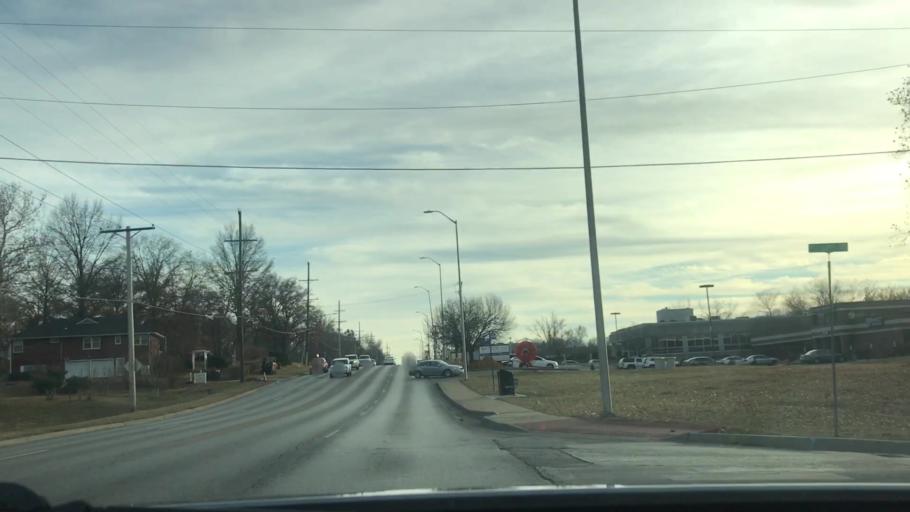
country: US
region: Missouri
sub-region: Clay County
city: Gladstone
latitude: 39.2047
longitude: -94.5764
